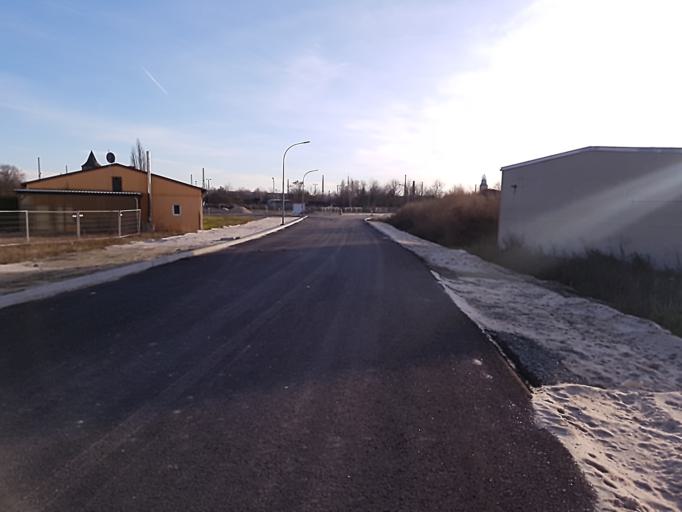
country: DE
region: Brandenburg
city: Finsterwalde
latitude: 51.6418
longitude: 13.7142
